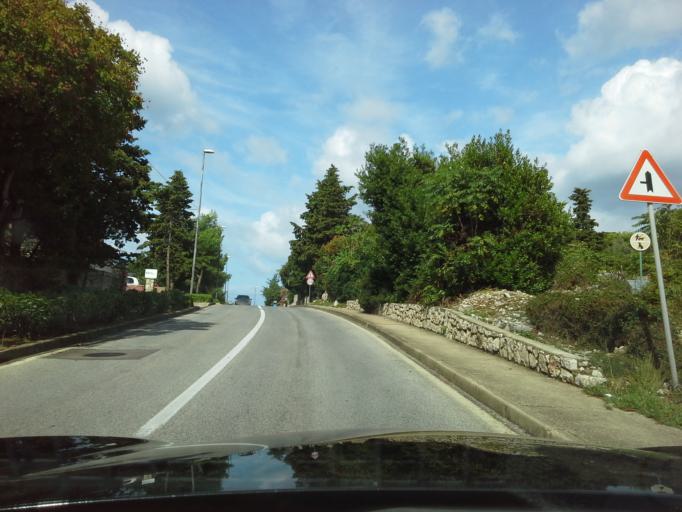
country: HR
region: Primorsko-Goranska
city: Mali Losinj
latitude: 44.5363
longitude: 14.4693
